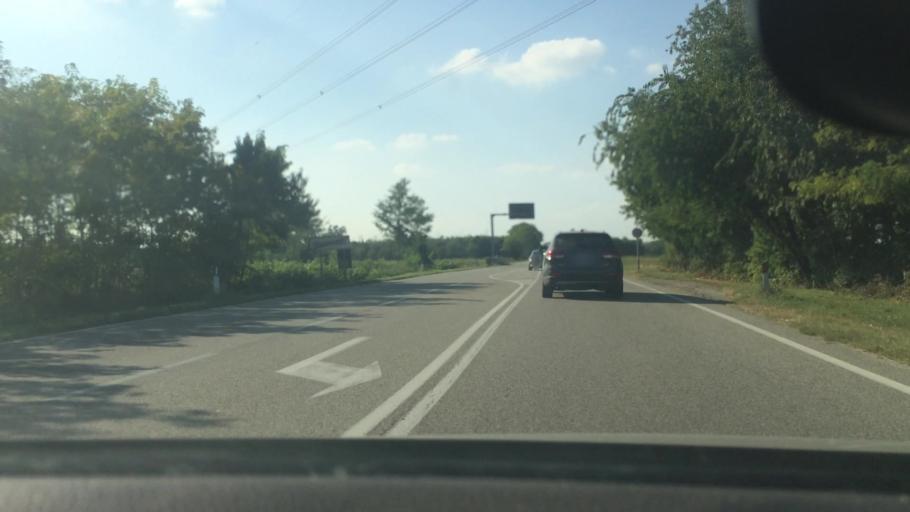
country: IT
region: Lombardy
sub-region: Citta metropolitana di Milano
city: Inveruno
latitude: 45.5251
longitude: 8.8492
